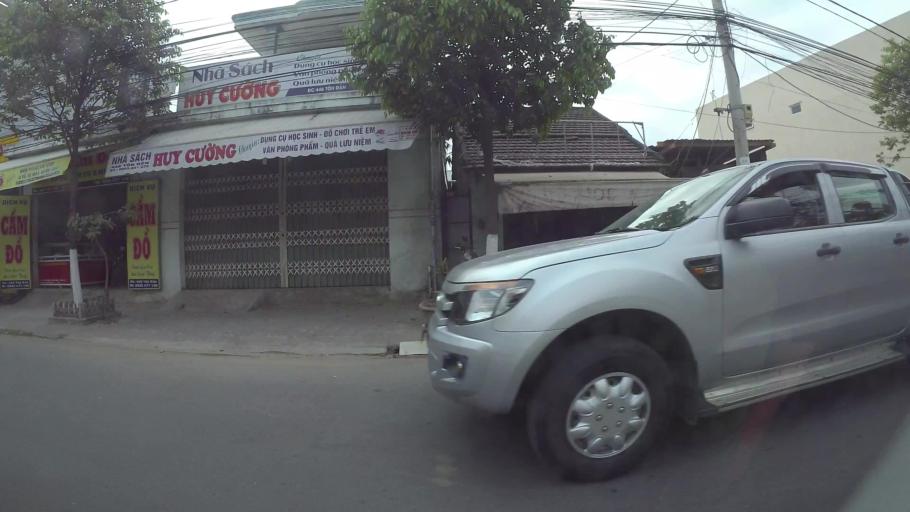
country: VN
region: Da Nang
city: Thanh Khe
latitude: 16.0434
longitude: 108.1829
